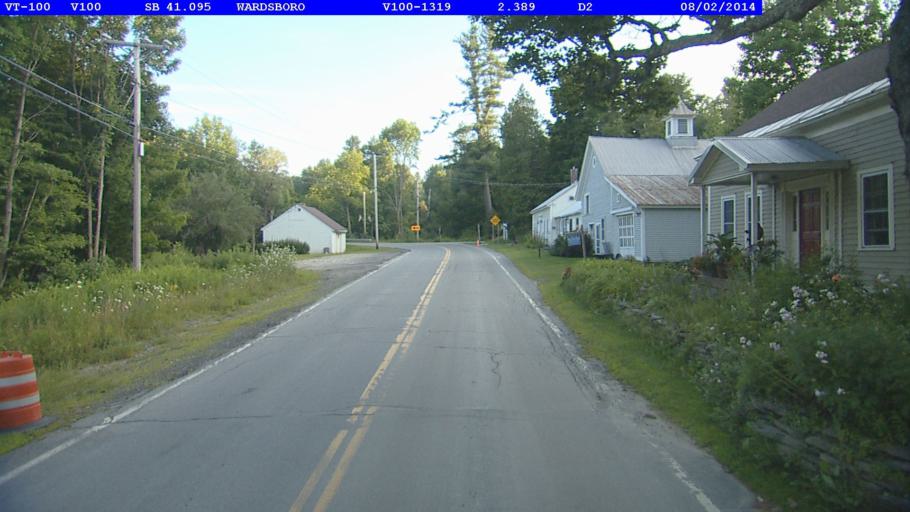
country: US
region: Vermont
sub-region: Windham County
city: Dover
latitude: 43.0312
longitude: -72.8513
